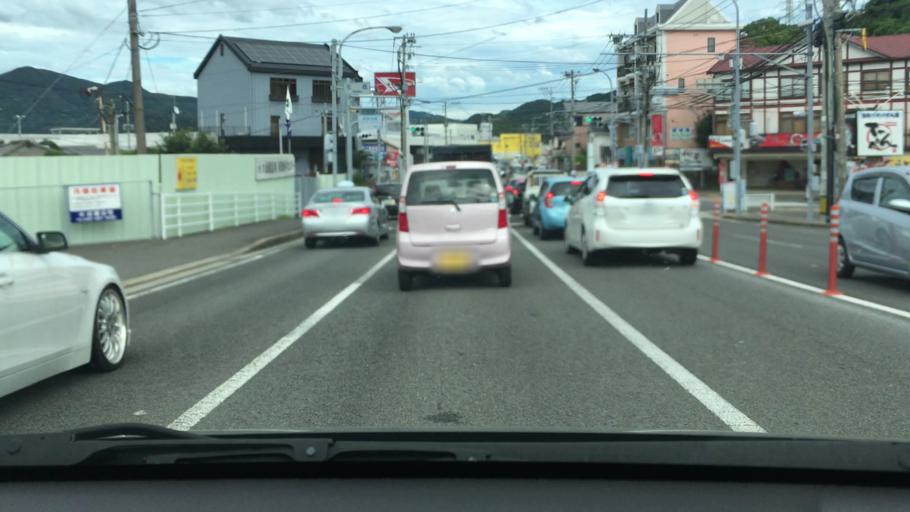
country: JP
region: Nagasaki
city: Togitsu
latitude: 32.8341
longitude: 129.8416
